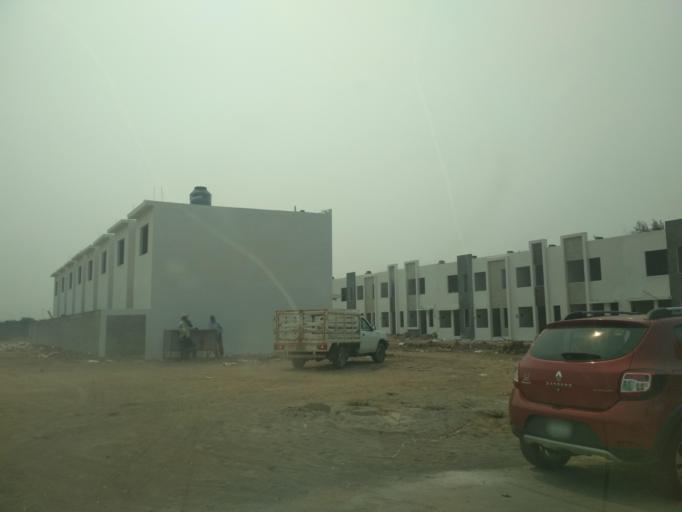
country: MX
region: Veracruz
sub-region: Veracruz
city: Las Amapolas
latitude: 19.1404
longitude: -96.2203
